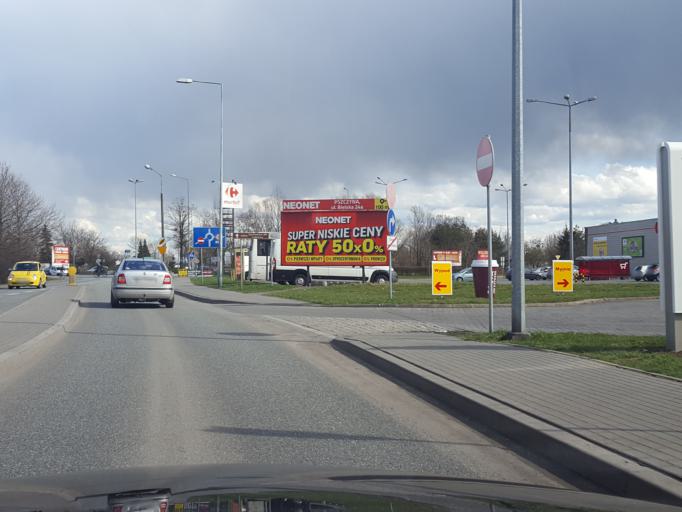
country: PL
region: Silesian Voivodeship
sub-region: Powiat pszczynski
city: Pszczyna
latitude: 49.9702
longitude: 18.9453
